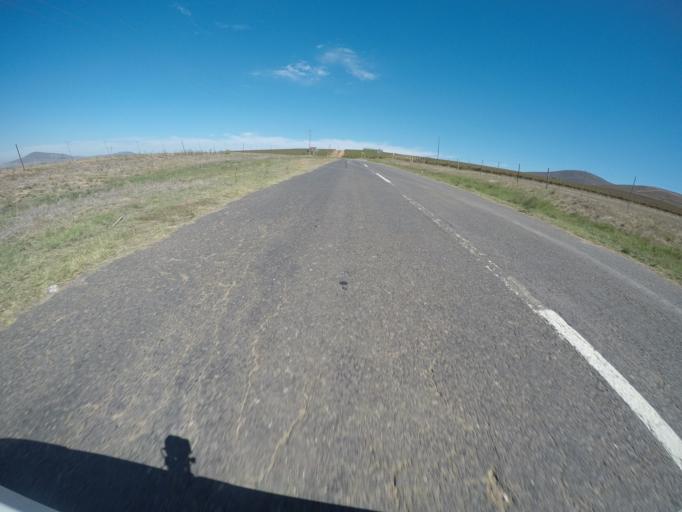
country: ZA
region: Western Cape
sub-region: City of Cape Town
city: Sunset Beach
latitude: -33.7096
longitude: 18.5833
